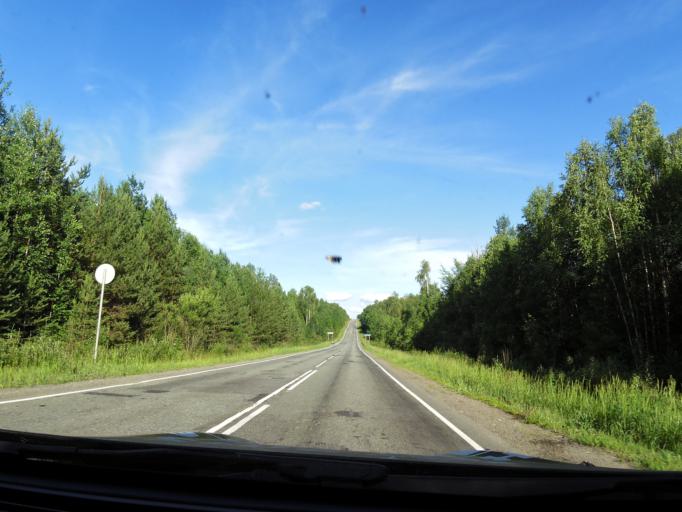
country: RU
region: Kirov
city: Chernaya Kholunitsa
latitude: 58.8649
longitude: 51.5805
